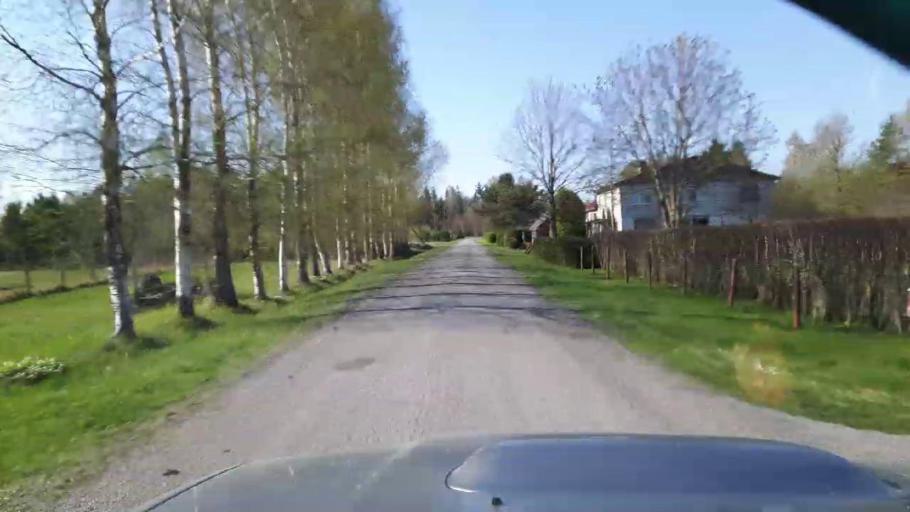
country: EE
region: Paernumaa
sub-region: Tootsi vald
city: Tootsi
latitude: 58.4871
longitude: 24.9068
